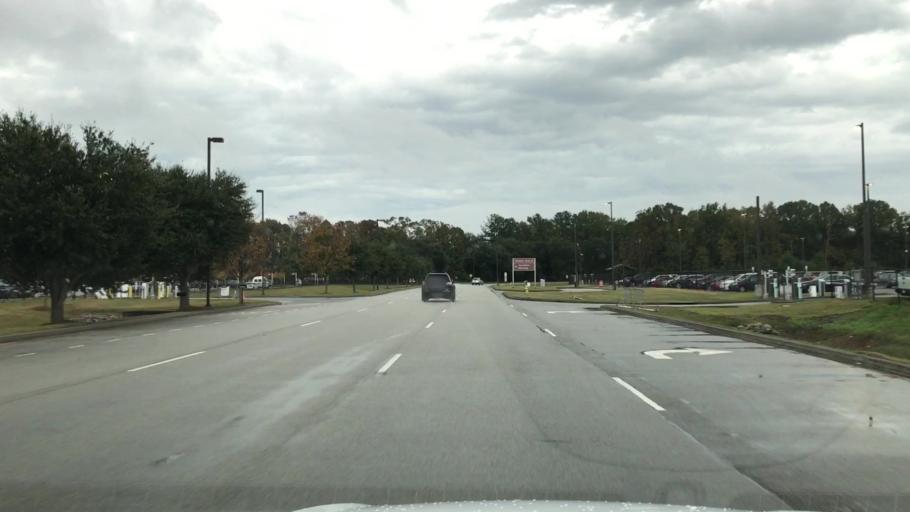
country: US
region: South Carolina
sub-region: Berkeley County
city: Hanahan
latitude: 32.8809
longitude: -80.0381
